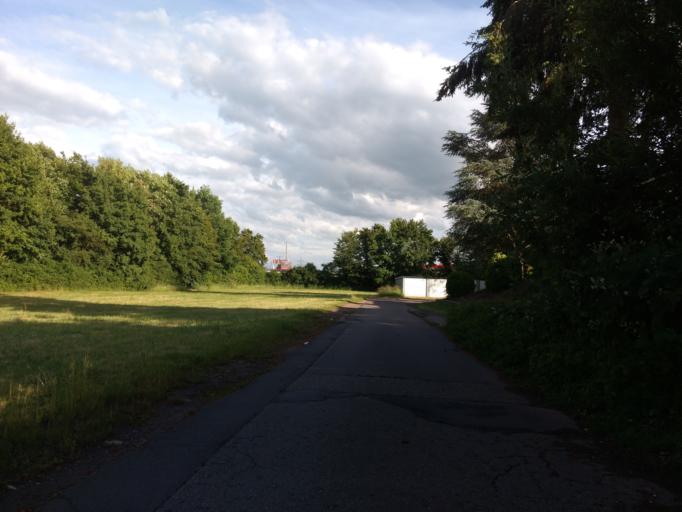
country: DE
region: Saarland
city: Merzig
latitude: 49.4432
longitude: 6.6222
